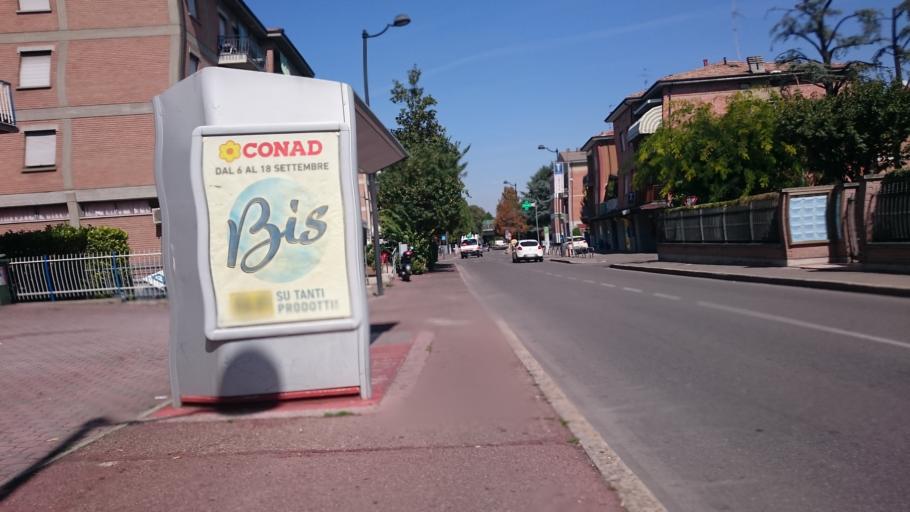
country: IT
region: Emilia-Romagna
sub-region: Provincia di Reggio Emilia
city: Reggio nell'Emilia
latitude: 44.7122
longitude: 10.6323
